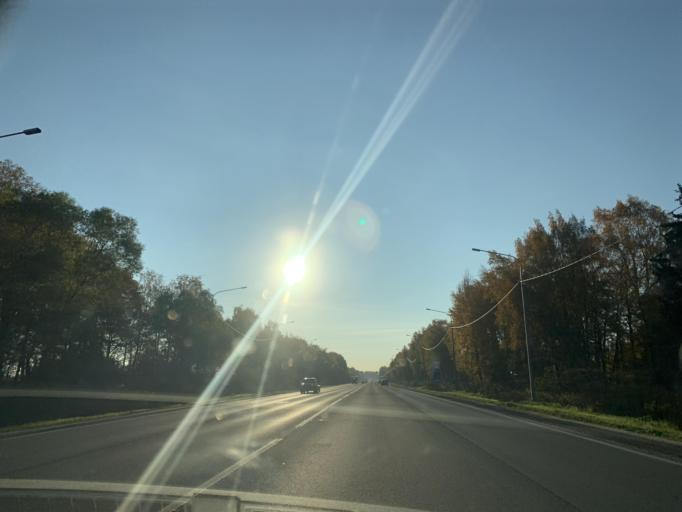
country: RU
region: Jaroslavl
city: Konstantinovskiy
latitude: 57.7473
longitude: 39.7109
